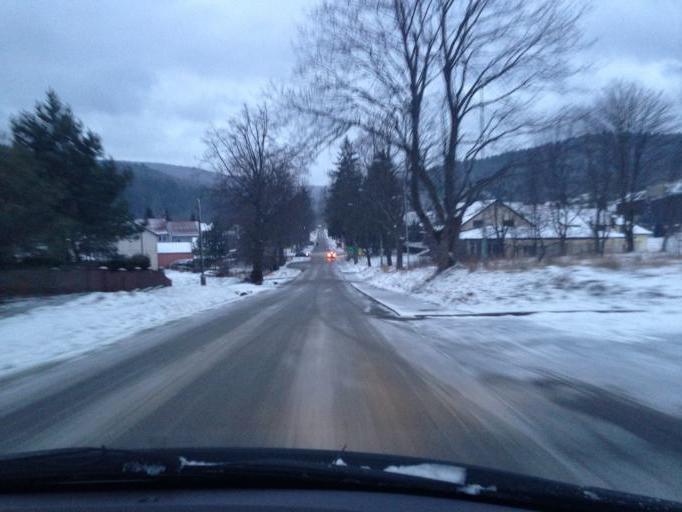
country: PL
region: Subcarpathian Voivodeship
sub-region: Powiat jasielski
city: Krempna
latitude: 49.5127
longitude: 21.5021
